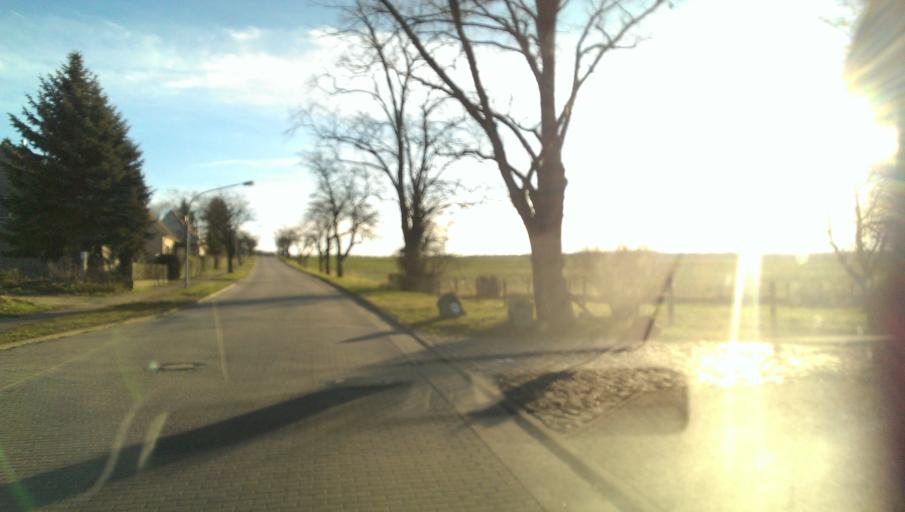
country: DE
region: Saxony-Anhalt
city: Eilsleben
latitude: 52.1125
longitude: 11.2013
